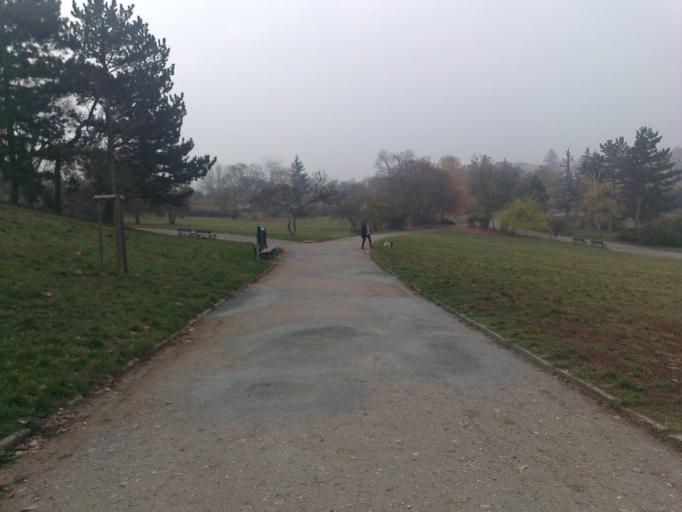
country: CZ
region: South Moravian
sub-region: Mesto Brno
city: Brno
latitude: 49.2034
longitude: 16.5840
